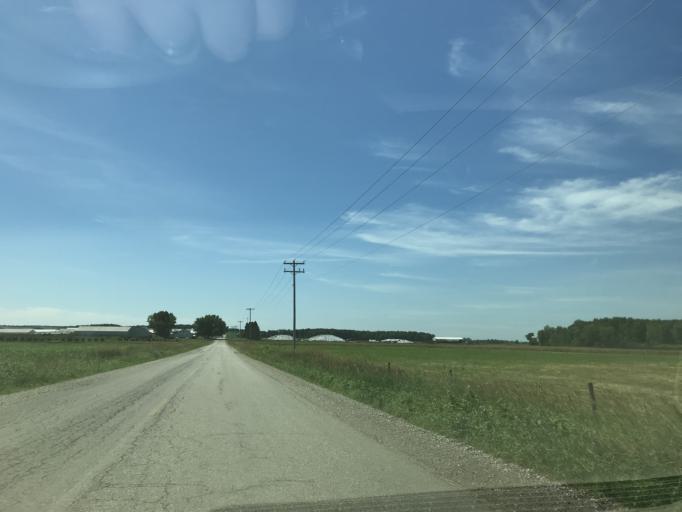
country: US
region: Michigan
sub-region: Missaukee County
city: Lake City
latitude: 44.3171
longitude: -85.0748
